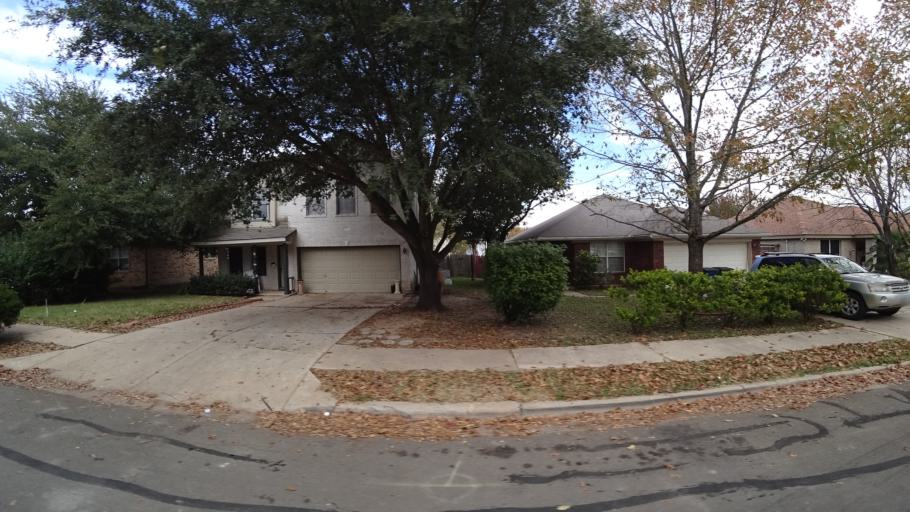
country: US
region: Texas
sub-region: Travis County
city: Onion Creek
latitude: 30.1584
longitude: -97.7375
